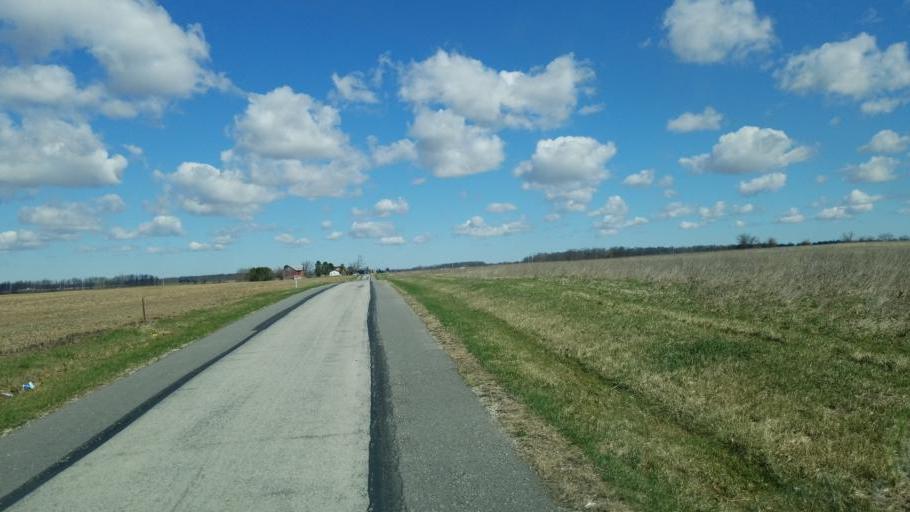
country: US
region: Ohio
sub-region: Sandusky County
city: Mount Carmel
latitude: 41.0900
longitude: -82.9383
